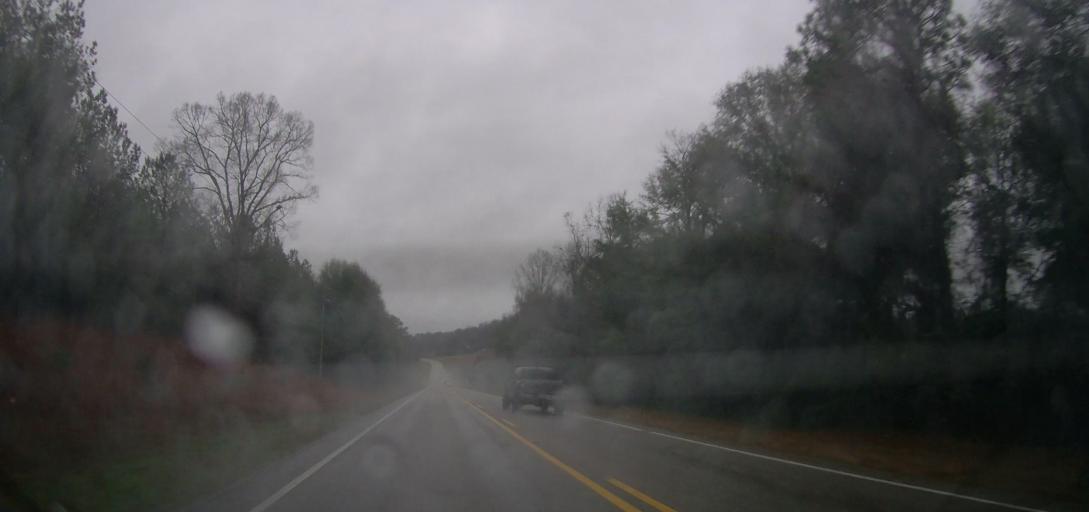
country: US
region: Alabama
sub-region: Autauga County
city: Pine Level
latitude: 32.5272
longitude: -86.6309
